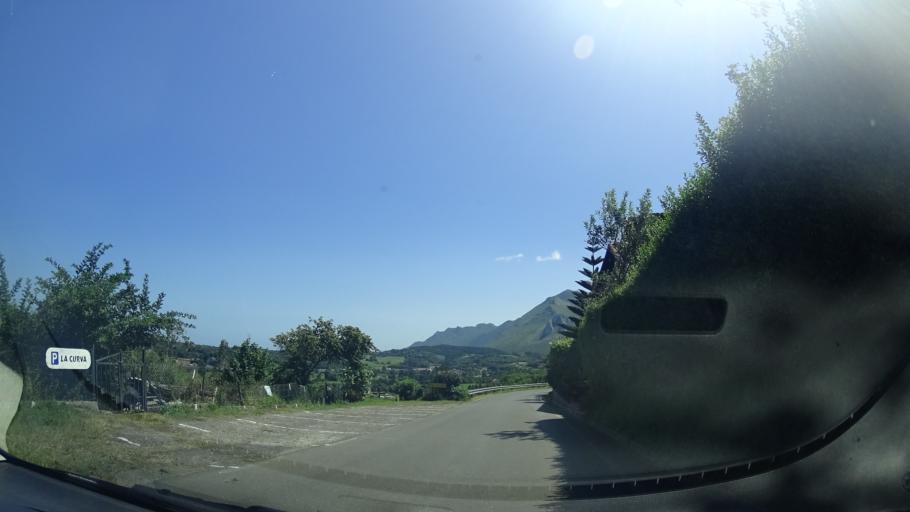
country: ES
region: Asturias
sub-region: Province of Asturias
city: Ribadesella
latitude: 43.4485
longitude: -5.0755
